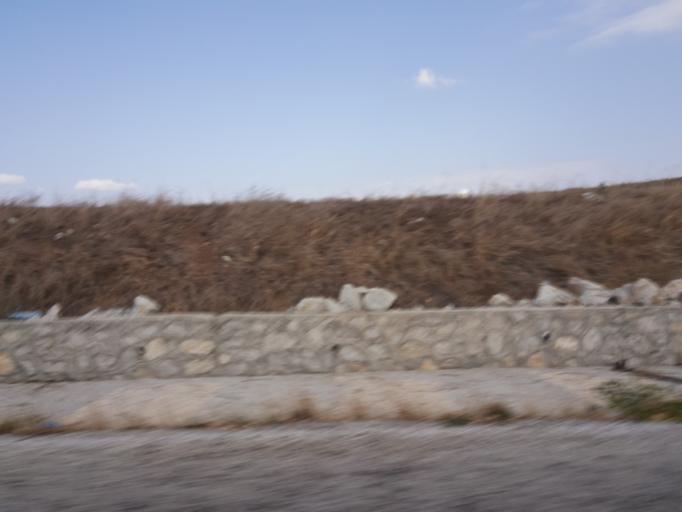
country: TR
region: Corum
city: Alaca
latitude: 40.1555
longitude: 34.7235
